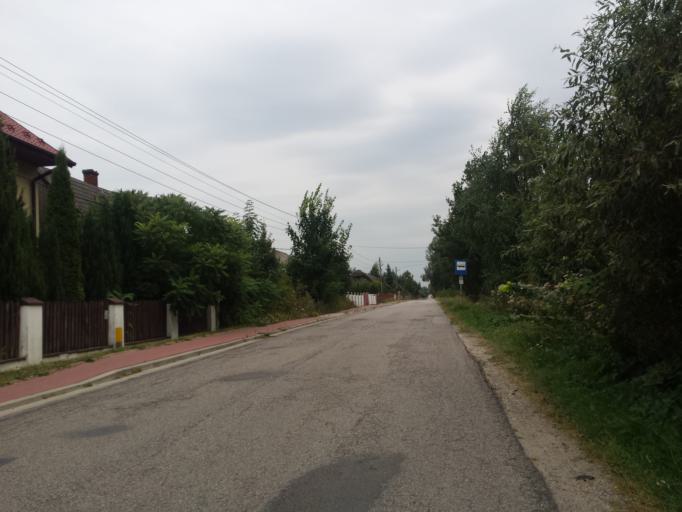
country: PL
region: Swietokrzyskie
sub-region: Powiat kielecki
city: Morawica
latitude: 50.7346
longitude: 20.6703
